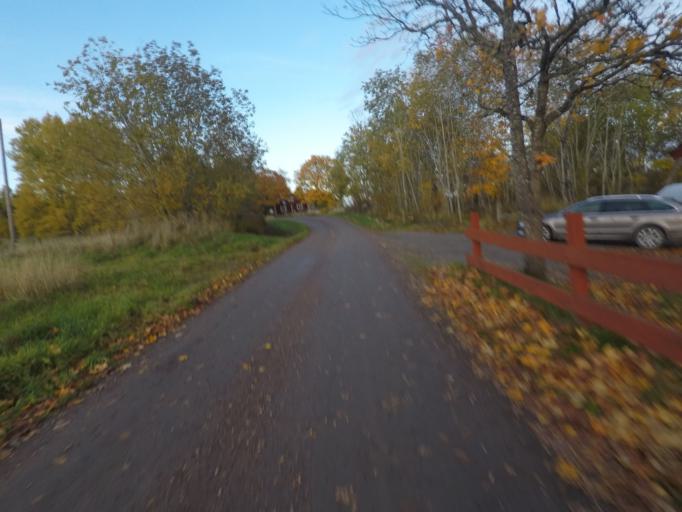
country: SE
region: OErebro
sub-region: Karlskoga Kommun
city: Karlskoga
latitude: 59.2965
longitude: 14.5078
